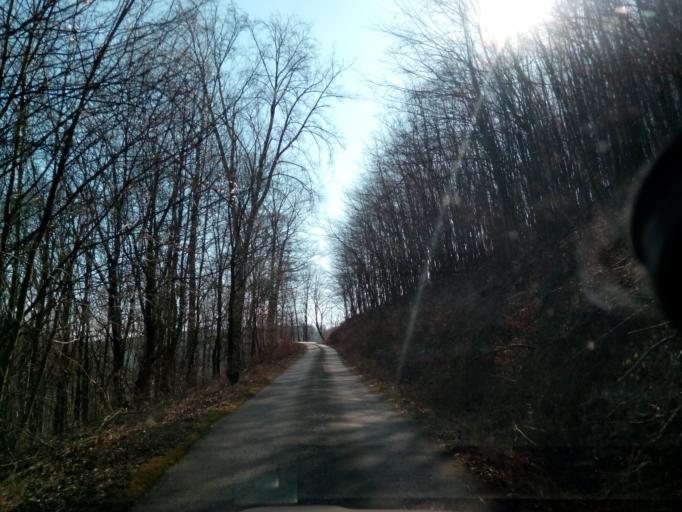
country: SK
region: Kosicky
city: Roznava
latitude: 48.5524
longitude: 20.5650
